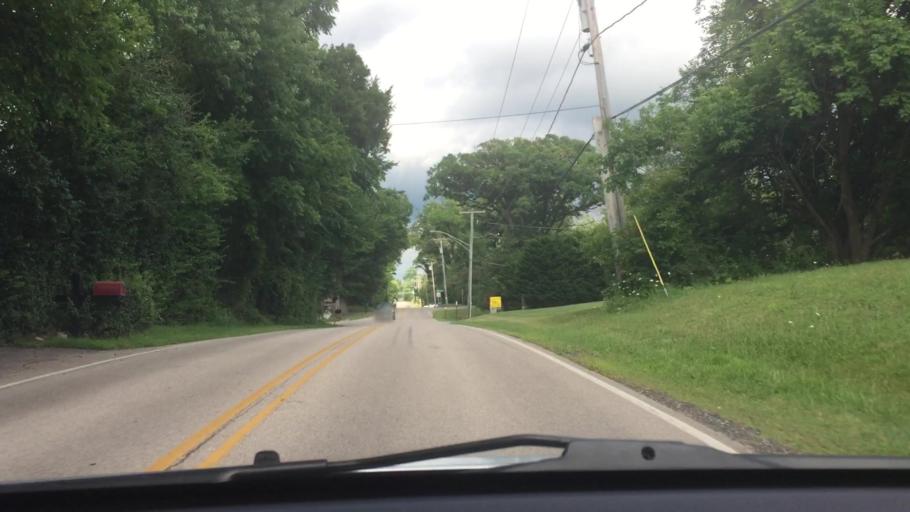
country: US
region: Illinois
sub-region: McHenry County
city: Crystal Lake
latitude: 42.2627
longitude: -88.3265
